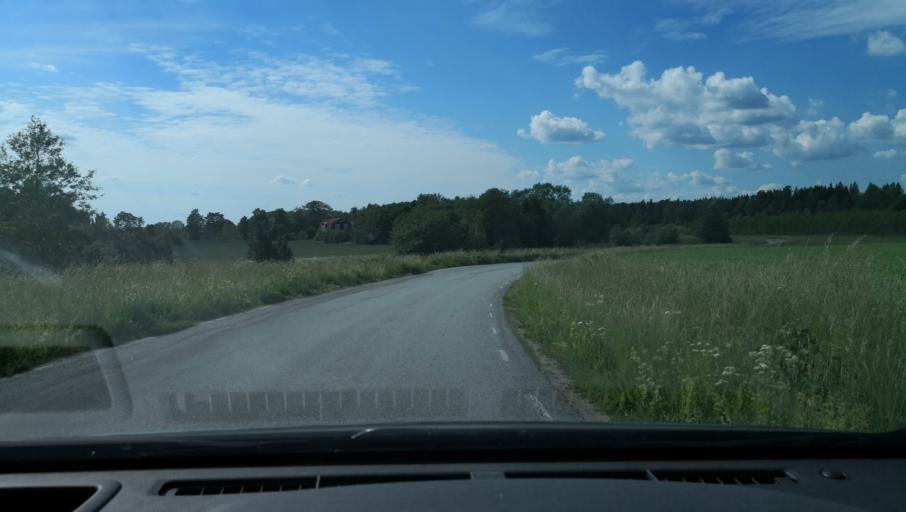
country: SE
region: Uppsala
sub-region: Enkopings Kommun
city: Orsundsbro
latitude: 59.8146
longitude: 17.3708
